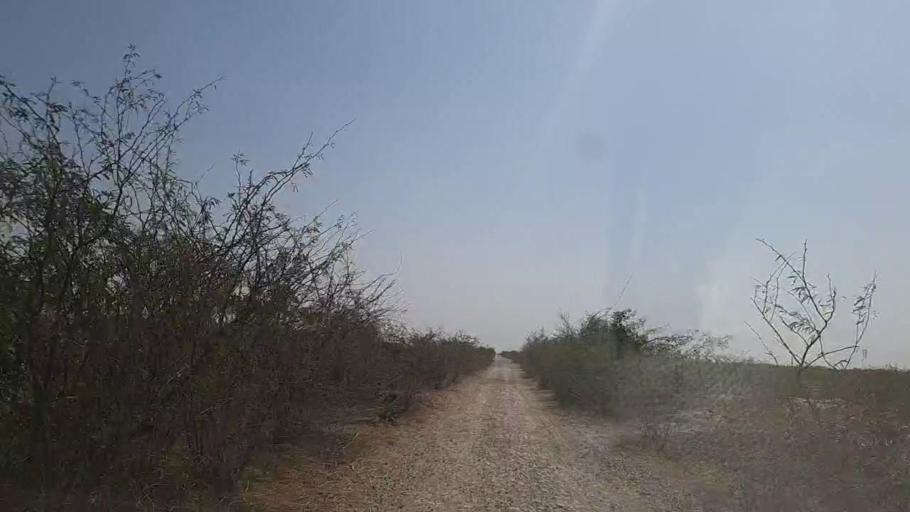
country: PK
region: Sindh
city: Naukot
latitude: 24.6399
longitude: 69.2741
